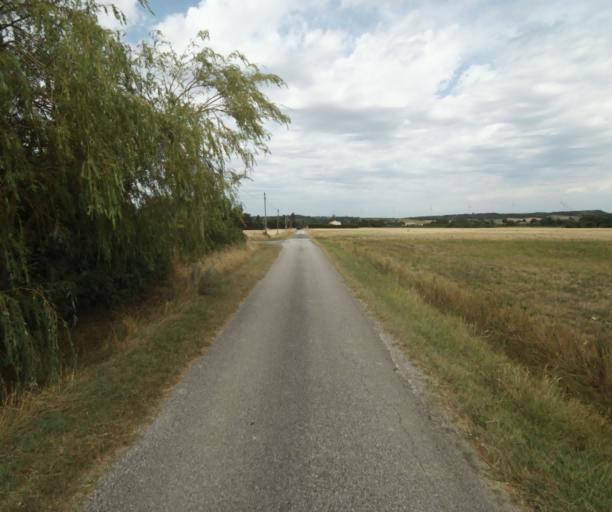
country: FR
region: Midi-Pyrenees
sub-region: Departement de la Haute-Garonne
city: Saint-Felix-Lauragais
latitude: 43.4398
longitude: 1.9308
